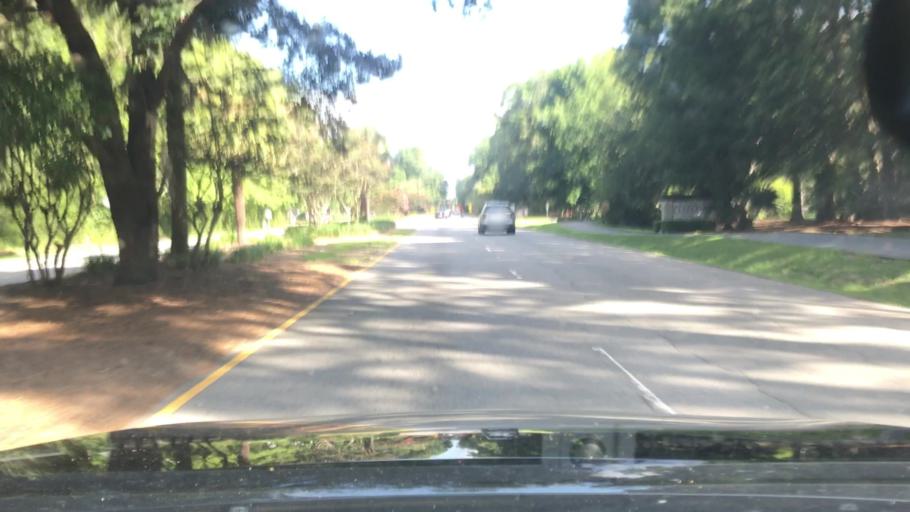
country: US
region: South Carolina
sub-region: Beaufort County
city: Hilton Head Island
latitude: 32.1493
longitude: -80.7574
